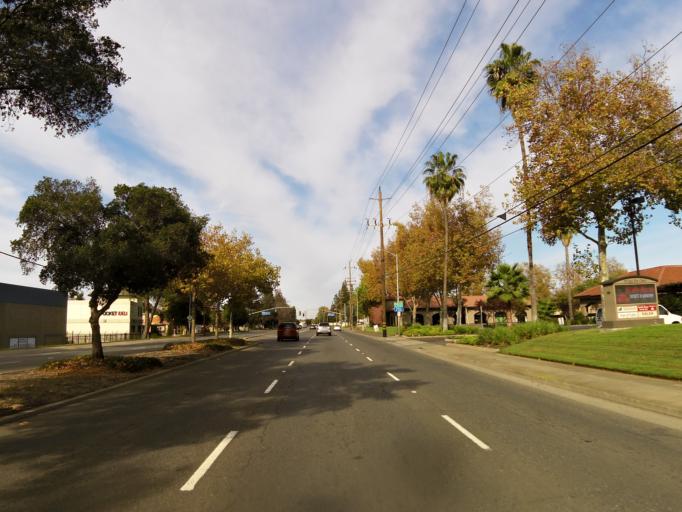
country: US
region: California
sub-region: Sacramento County
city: Gold River
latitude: 38.5965
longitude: -121.2656
